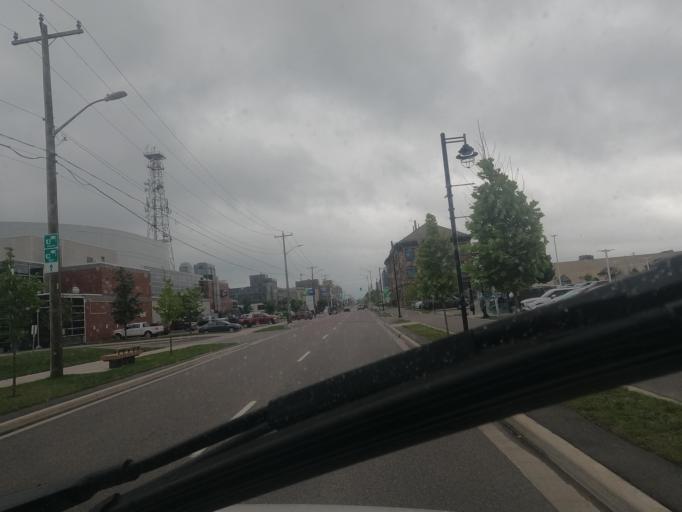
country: CA
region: Ontario
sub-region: Algoma
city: Sault Ste. Marie
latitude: 46.5137
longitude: -84.3379
